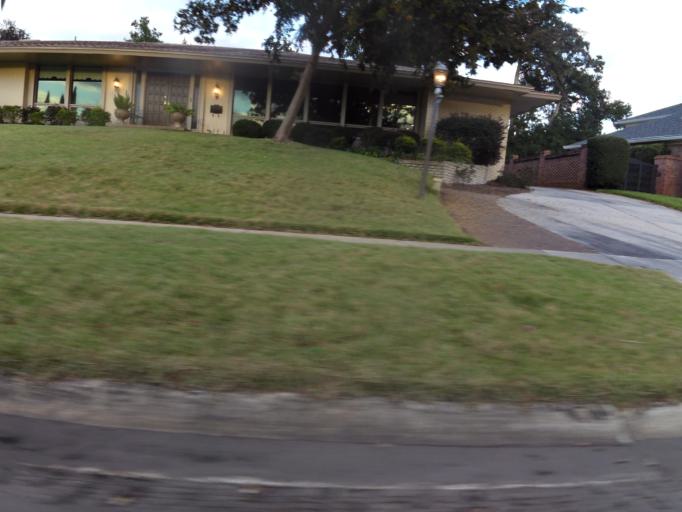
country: US
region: Florida
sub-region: Duval County
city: Jacksonville
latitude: 30.2780
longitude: -81.6633
